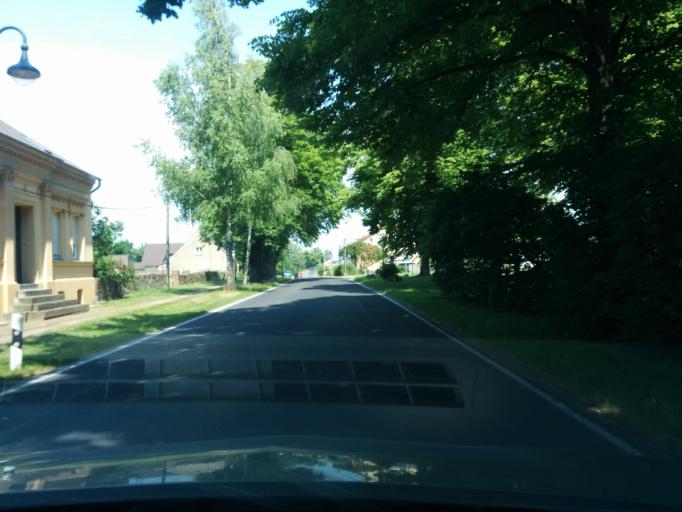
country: DE
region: Brandenburg
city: Ahrensfelde
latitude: 52.6282
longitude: 13.5744
